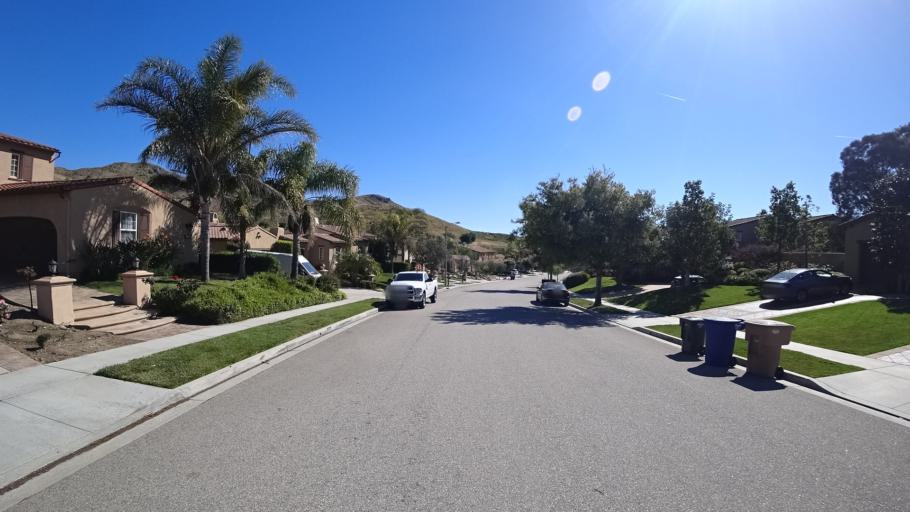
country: US
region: California
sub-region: Ventura County
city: Casa Conejo
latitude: 34.1742
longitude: -118.9888
